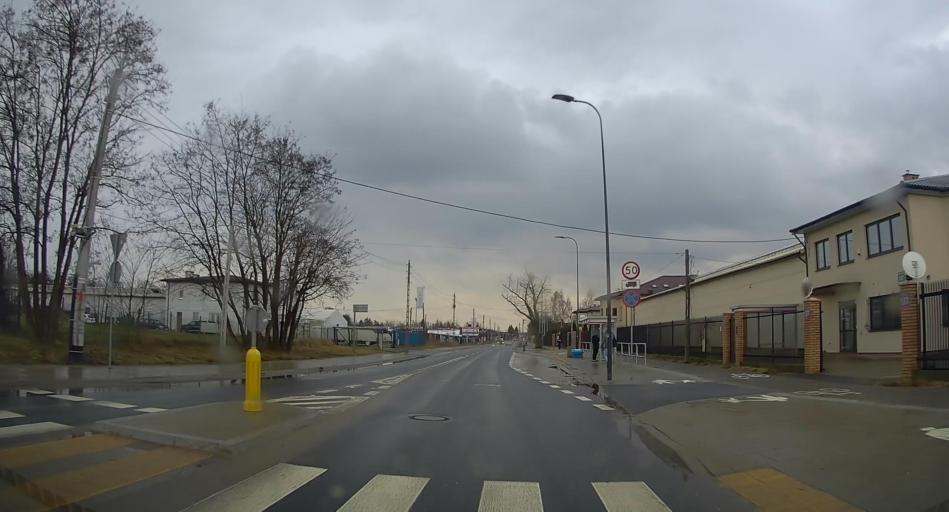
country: PL
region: Masovian Voivodeship
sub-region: Warszawa
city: Wawer
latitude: 52.1935
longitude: 21.1383
